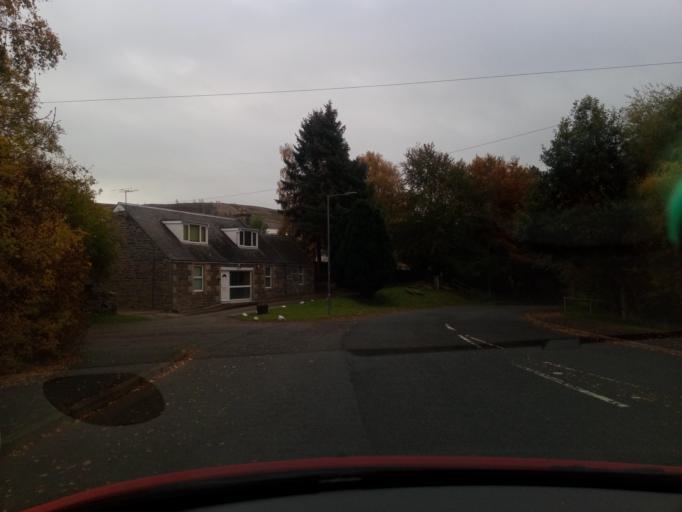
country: GB
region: Scotland
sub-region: The Scottish Borders
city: Galashiels
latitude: 55.6173
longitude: -2.8771
